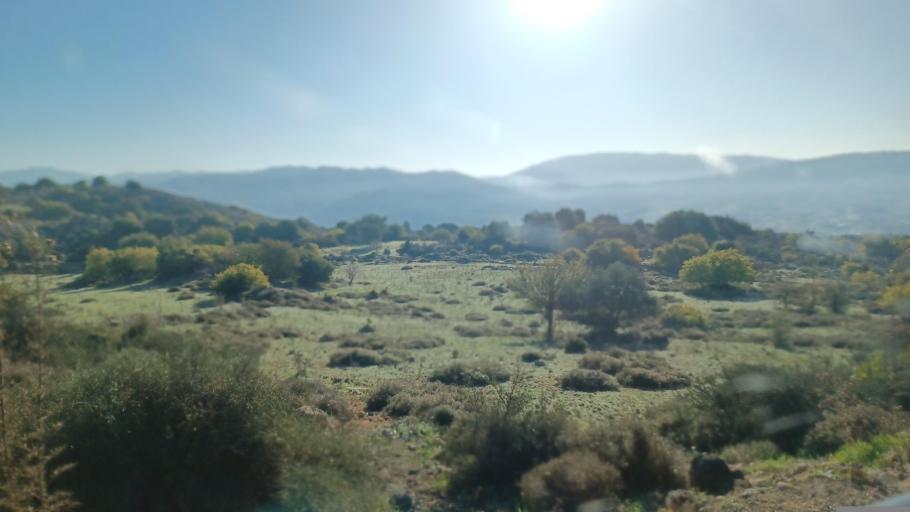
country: CY
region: Pafos
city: Polis
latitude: 34.9847
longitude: 32.5123
